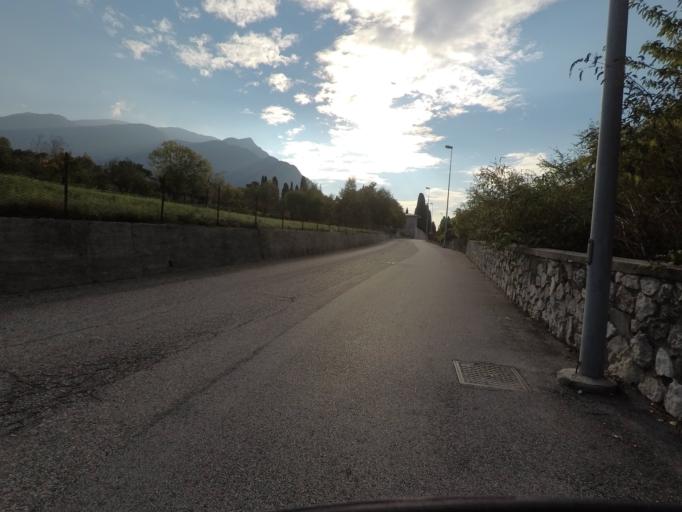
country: IT
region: Friuli Venezia Giulia
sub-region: Provincia di Udine
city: Gemona
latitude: 46.2841
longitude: 13.1289
